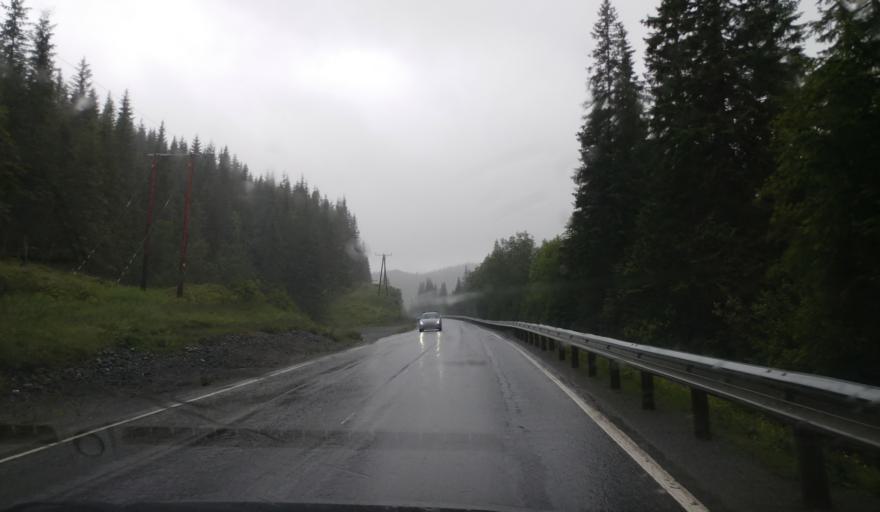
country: NO
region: Sor-Trondelag
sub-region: Selbu
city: Mebonden
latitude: 63.3458
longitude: 11.0765
